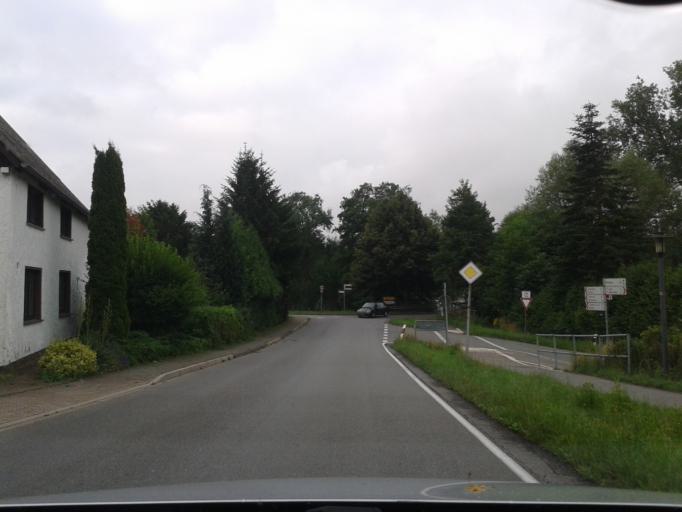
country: DE
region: North Rhine-Westphalia
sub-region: Regierungsbezirk Detmold
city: Dorentrup
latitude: 52.0104
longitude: 8.9598
